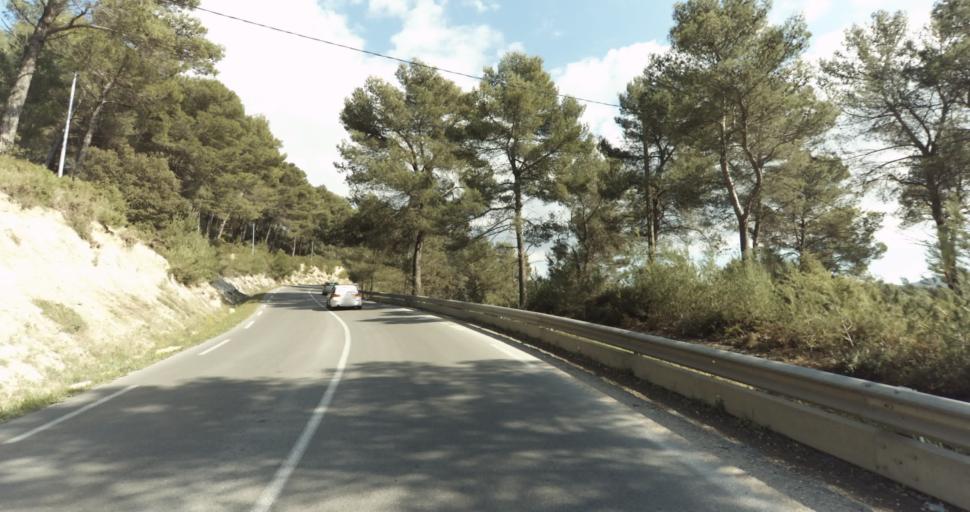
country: FR
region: Provence-Alpes-Cote d'Azur
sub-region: Departement des Bouches-du-Rhone
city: Gardanne
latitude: 43.4498
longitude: 5.5022
